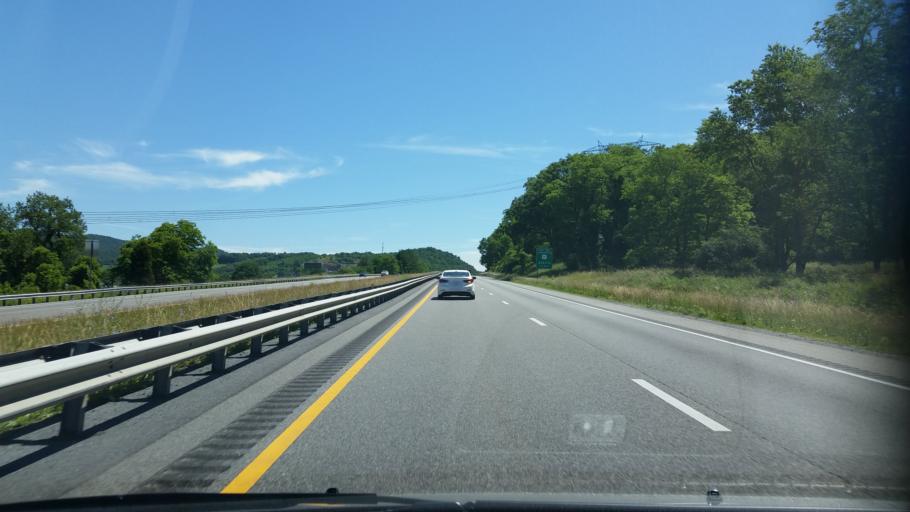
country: US
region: Virginia
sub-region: Smyth County
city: Atkins
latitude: 36.8597
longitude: -81.4531
